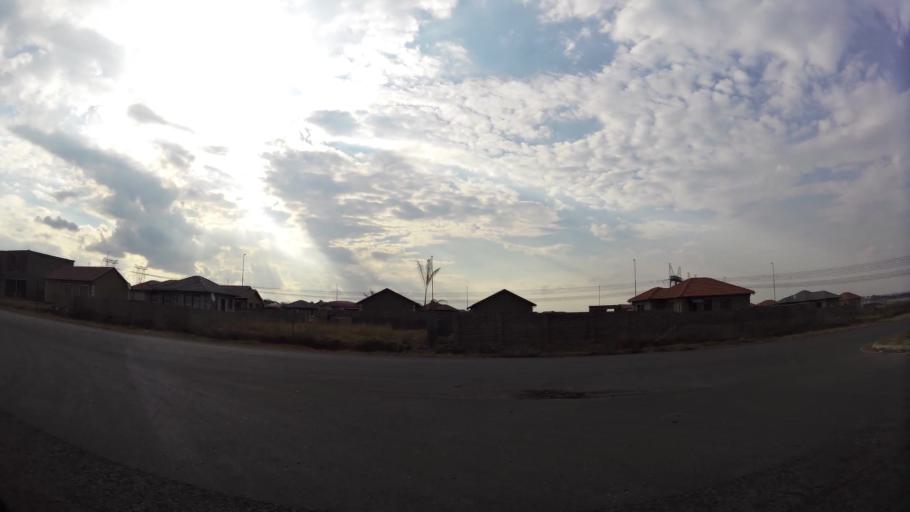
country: ZA
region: Gauteng
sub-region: Sedibeng District Municipality
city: Vereeniging
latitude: -26.6965
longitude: 27.8864
